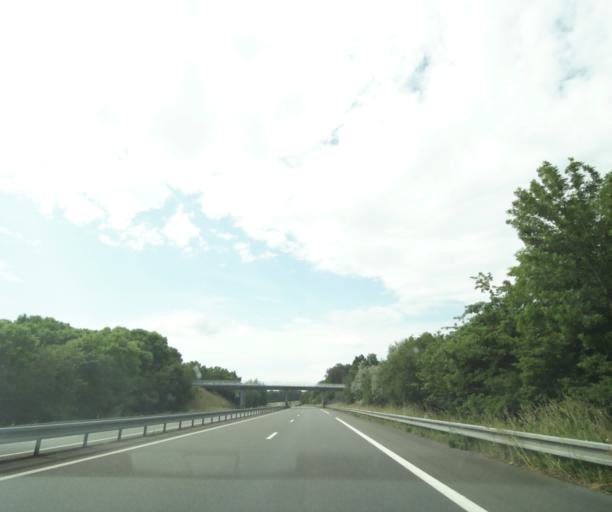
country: FR
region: Pays de la Loire
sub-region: Departement de Maine-et-Loire
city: Brion
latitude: 47.4259
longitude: -0.1448
